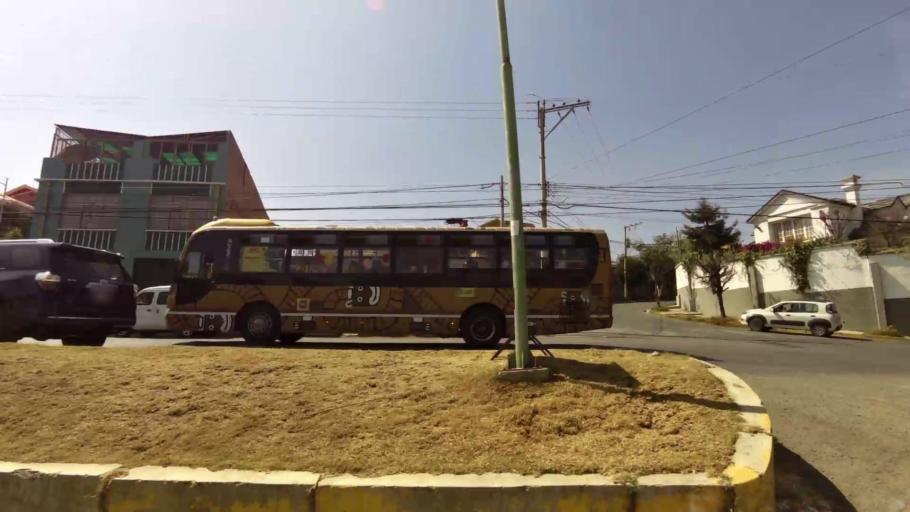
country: BO
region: La Paz
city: La Paz
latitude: -16.5430
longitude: -68.0652
